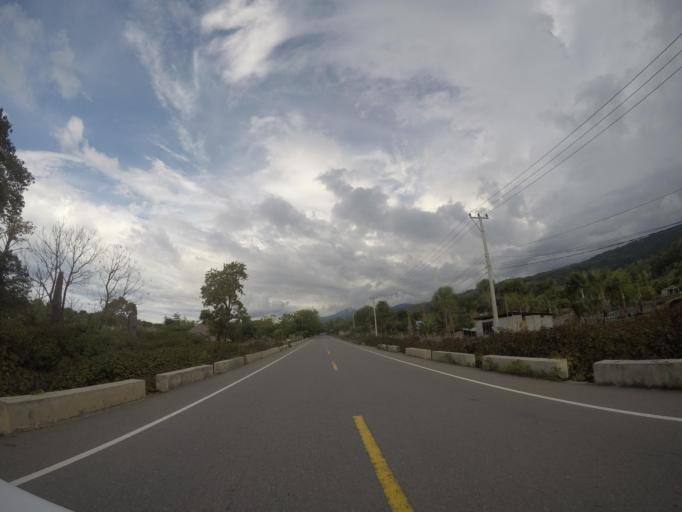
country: TL
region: Liquica
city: Maubara
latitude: -8.6059
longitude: 125.2563
